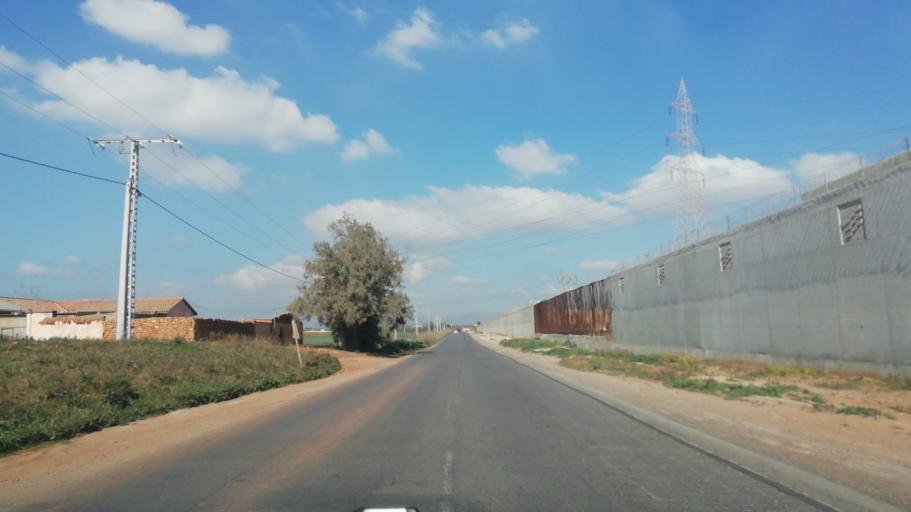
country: DZ
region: Oran
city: Ain el Bya
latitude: 35.7519
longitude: -0.2667
